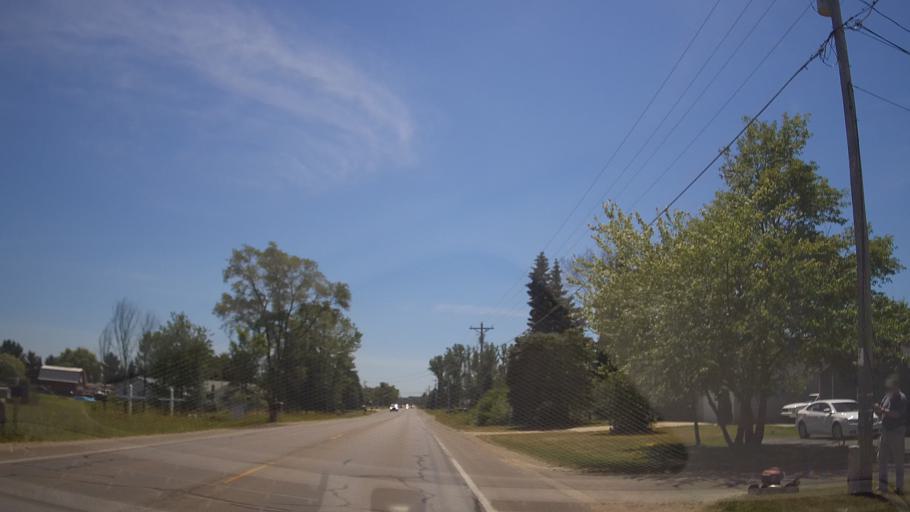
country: US
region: Michigan
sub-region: Grand Traverse County
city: Traverse City
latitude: 44.6762
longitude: -85.6899
